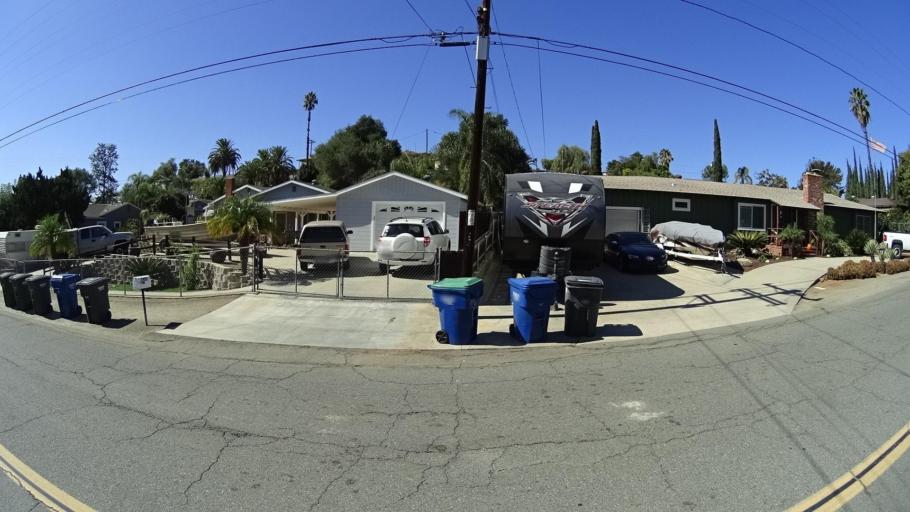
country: US
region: California
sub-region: San Diego County
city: Bostonia
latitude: 32.8162
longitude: -116.9301
